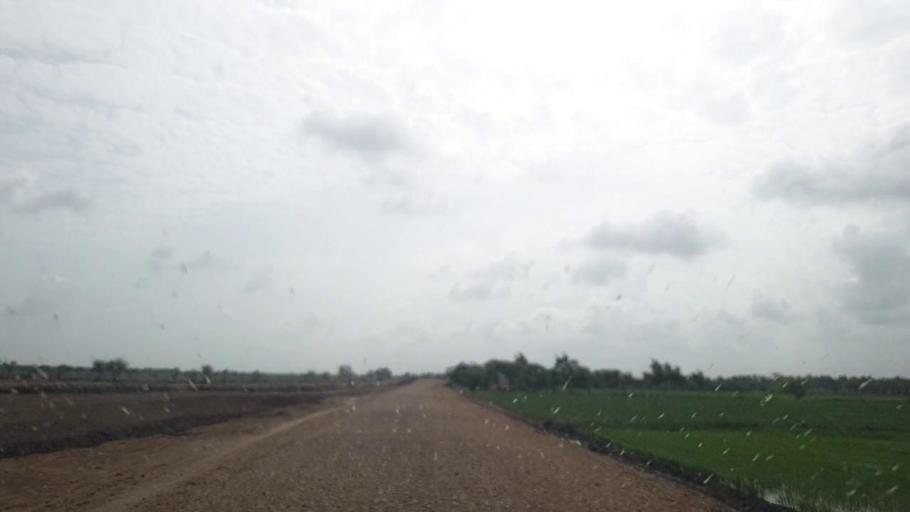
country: PK
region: Sindh
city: Tando Bago
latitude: 24.8042
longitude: 69.0137
